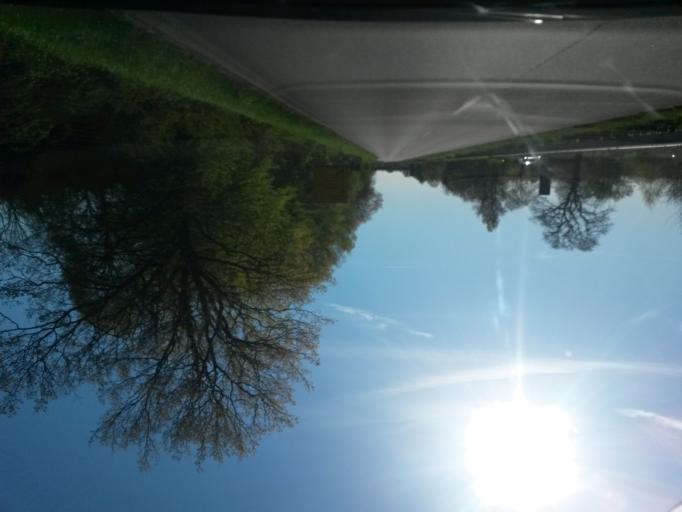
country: DE
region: Schleswig-Holstein
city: Rellingen
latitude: 53.6102
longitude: 9.8086
